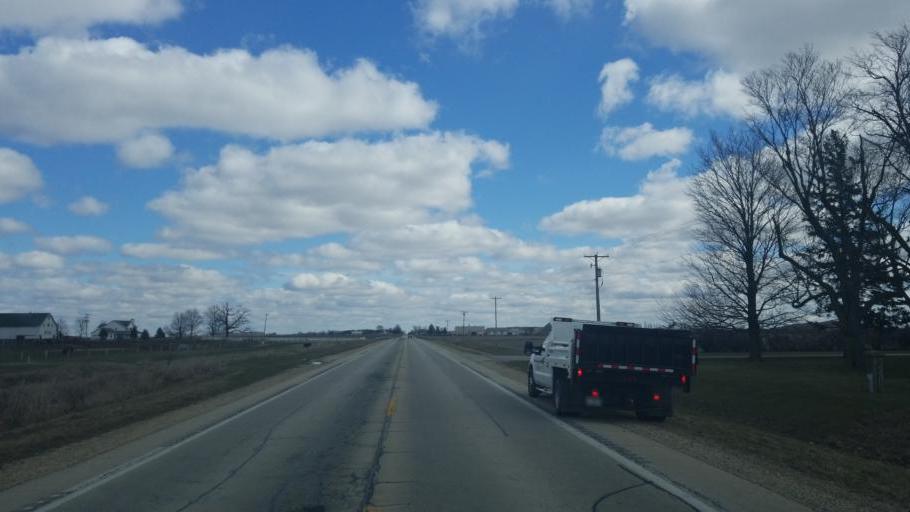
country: US
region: Illinois
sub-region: Douglas County
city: Tuscola
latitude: 39.7916
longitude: -88.2556
